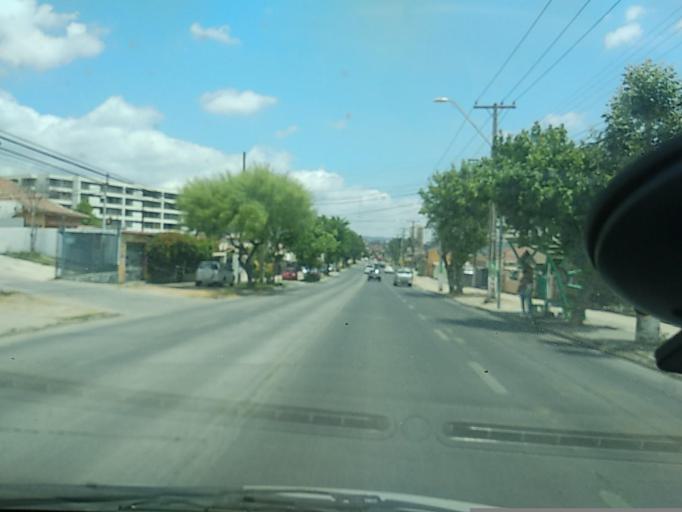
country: CL
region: Valparaiso
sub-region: Provincia de Marga Marga
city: Quilpue
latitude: -33.0426
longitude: -71.4314
